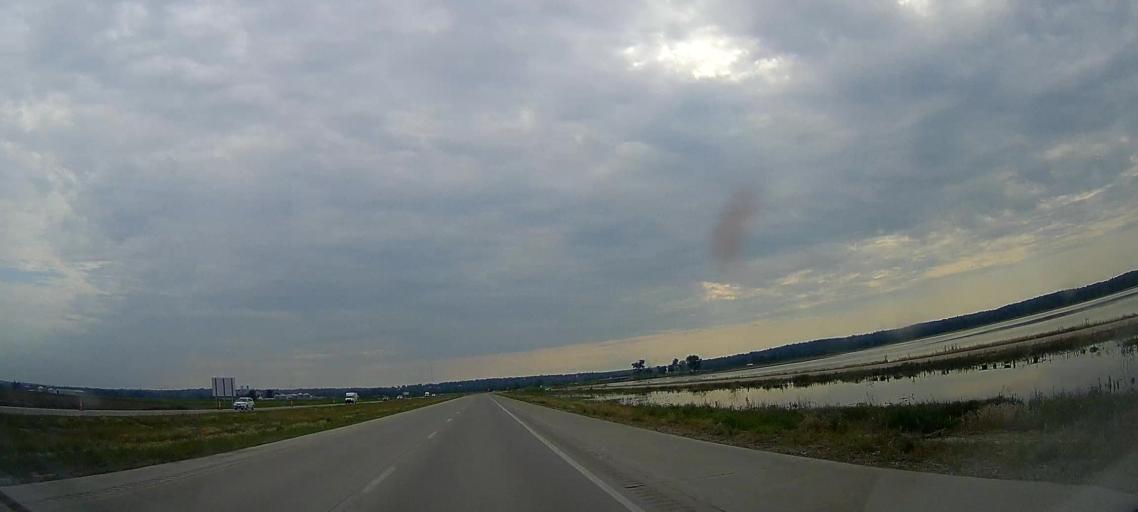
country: US
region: Iowa
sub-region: Pottawattamie County
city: Carter Lake
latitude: 41.3488
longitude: -95.9191
